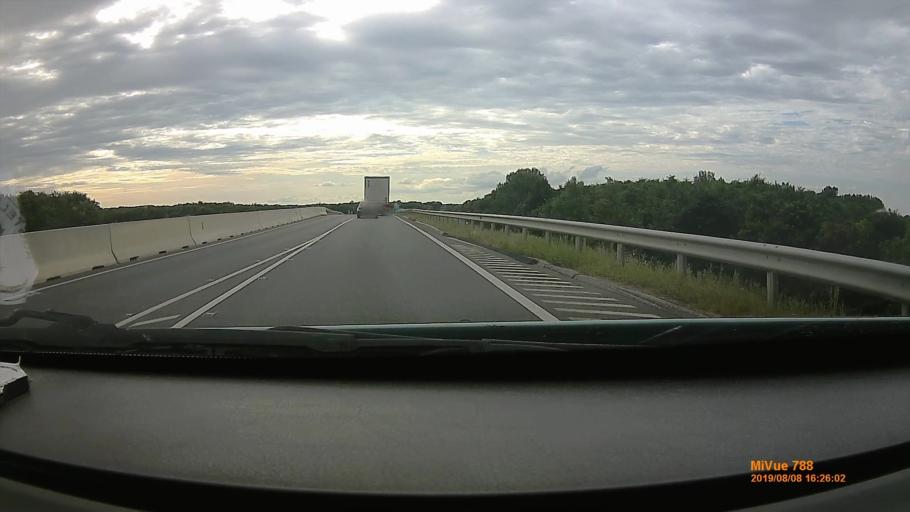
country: HU
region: Szabolcs-Szatmar-Bereg
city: Vaja
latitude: 47.9712
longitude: 22.2065
